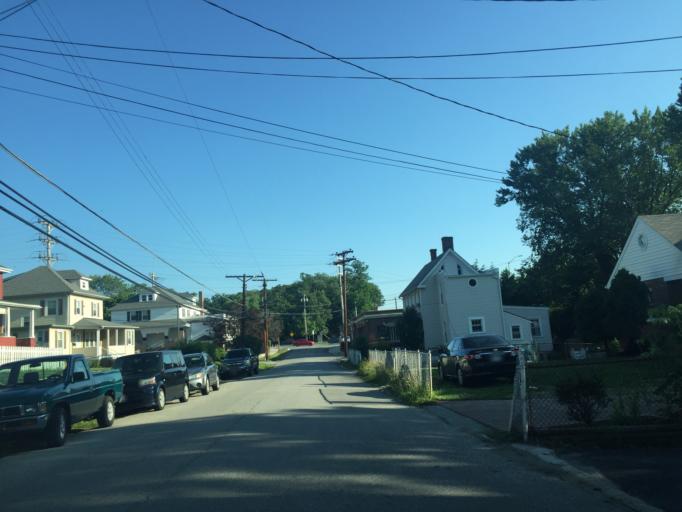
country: US
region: Maryland
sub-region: Baltimore County
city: Catonsville
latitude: 39.2723
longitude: -76.7248
